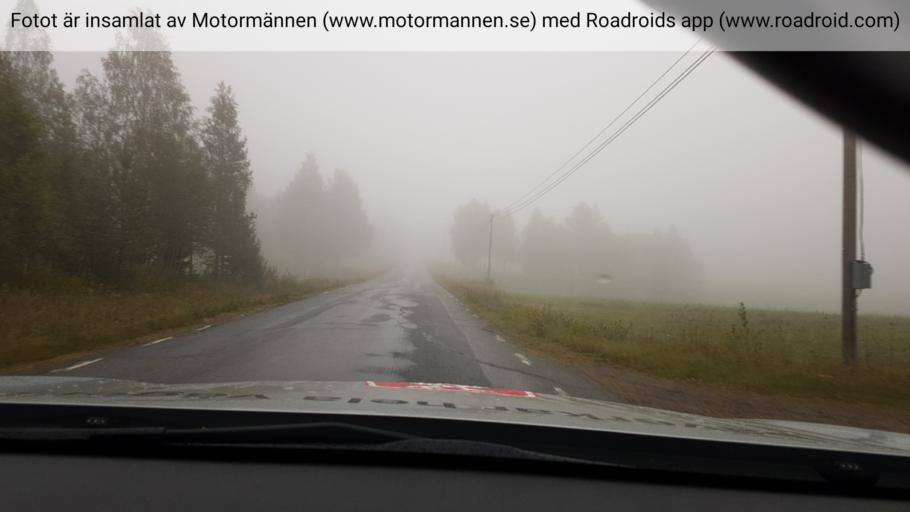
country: SE
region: Vaesterbotten
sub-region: Vannas Kommun
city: Vannasby
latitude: 64.0770
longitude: 20.0581
